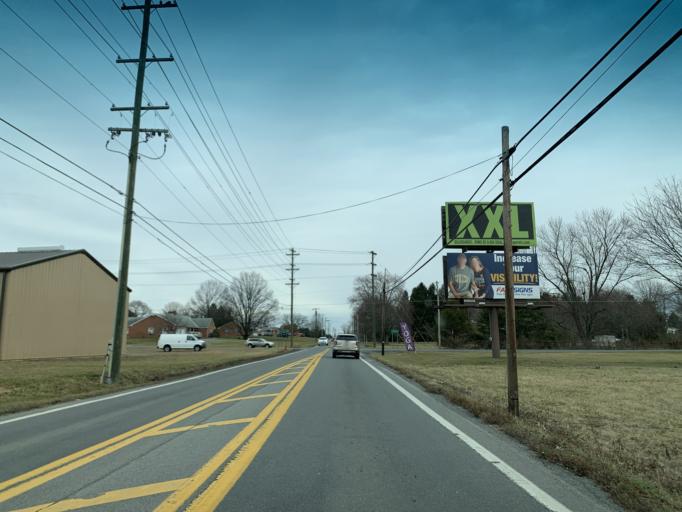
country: US
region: Maryland
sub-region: Washington County
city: Williamsport
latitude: 39.5899
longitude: -77.8565
